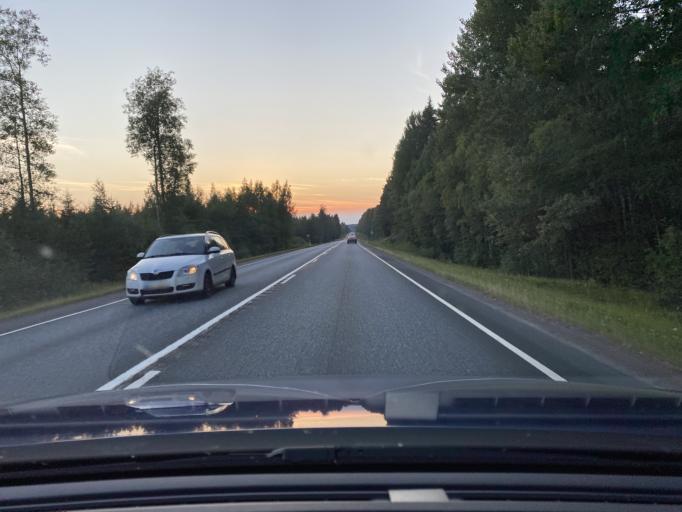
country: FI
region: Pirkanmaa
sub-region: Luoteis-Pirkanmaa
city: Ikaalinen
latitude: 61.7938
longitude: 22.9831
